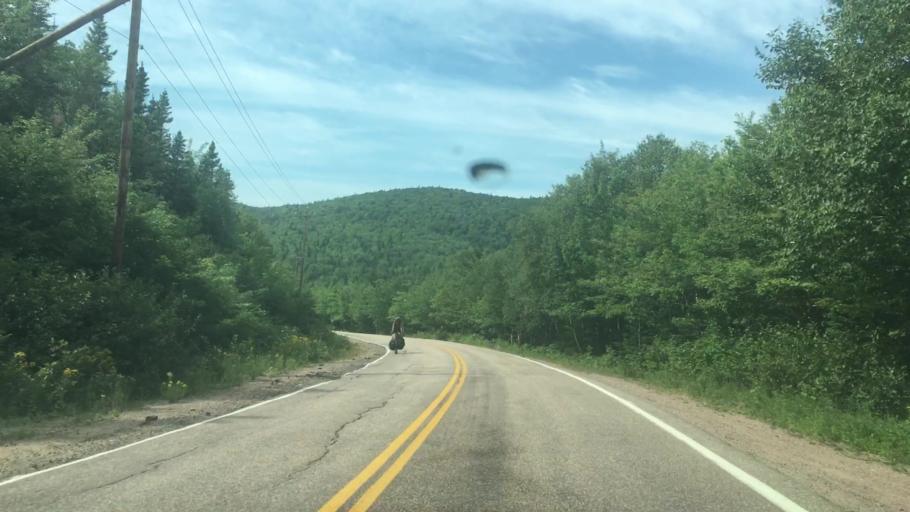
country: CA
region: Nova Scotia
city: Sydney Mines
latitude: 46.6055
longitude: -60.3910
